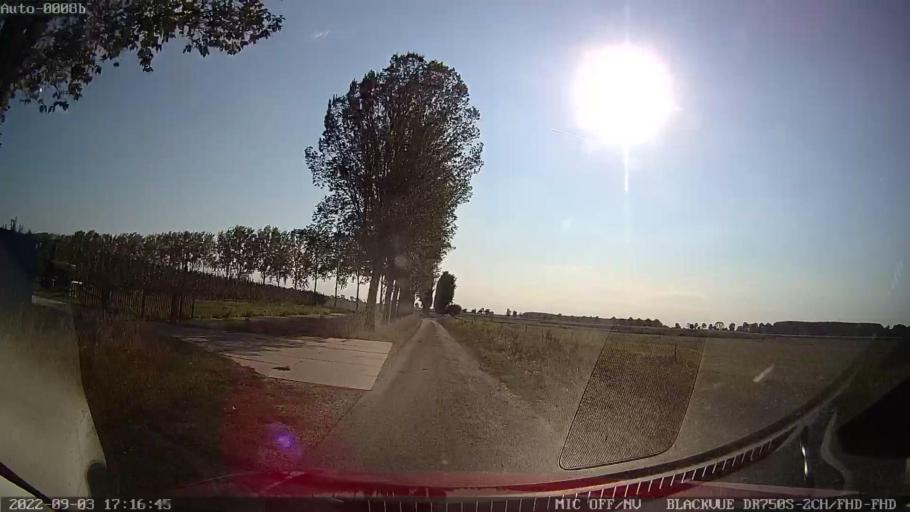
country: NL
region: Gelderland
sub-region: Gemeente Buren
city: Lienden
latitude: 51.9479
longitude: 5.4843
